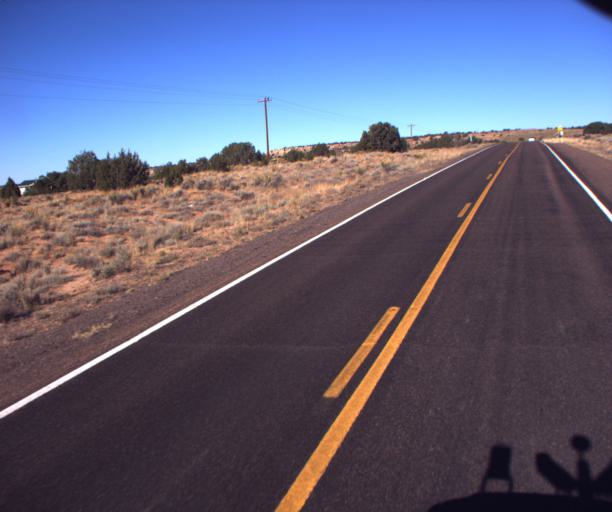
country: US
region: Arizona
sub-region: Navajo County
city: First Mesa
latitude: 35.7607
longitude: -110.1461
